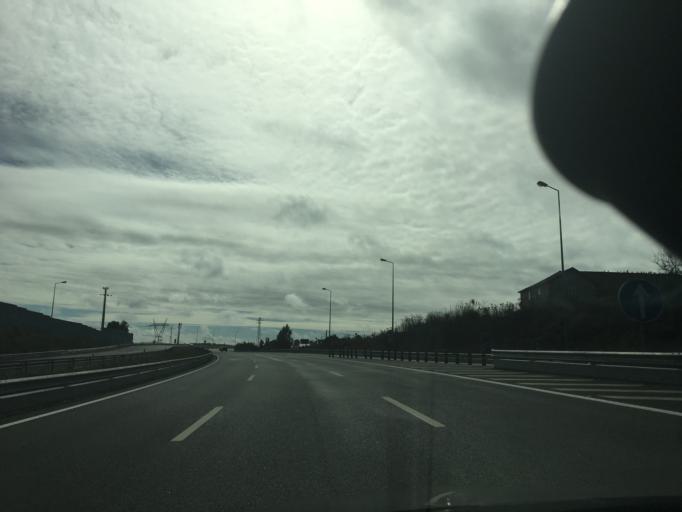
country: PT
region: Porto
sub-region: Matosinhos
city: Santa Cruz do Bispo
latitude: 41.2352
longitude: -8.6541
